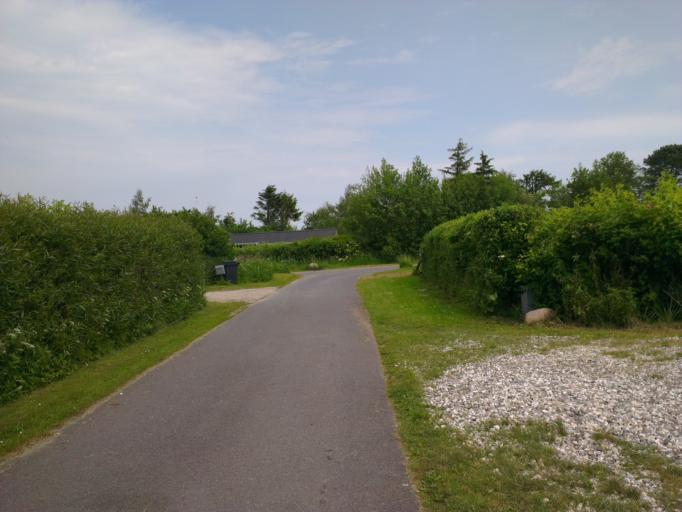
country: DK
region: Capital Region
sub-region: Frederikssund Kommune
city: Jaegerspris
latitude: 55.8355
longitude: 11.9548
